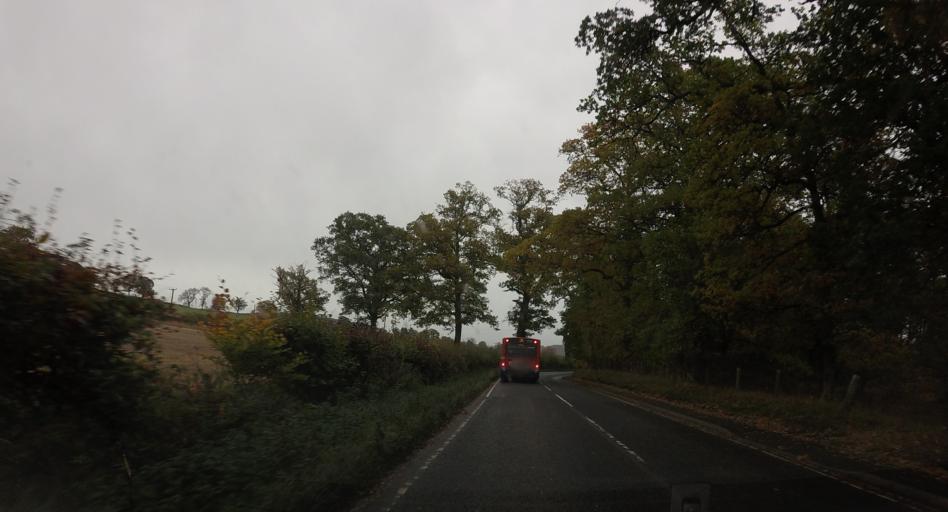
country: GB
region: Scotland
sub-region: Perth and Kinross
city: Bankfoot
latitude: 56.5466
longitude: -3.4730
